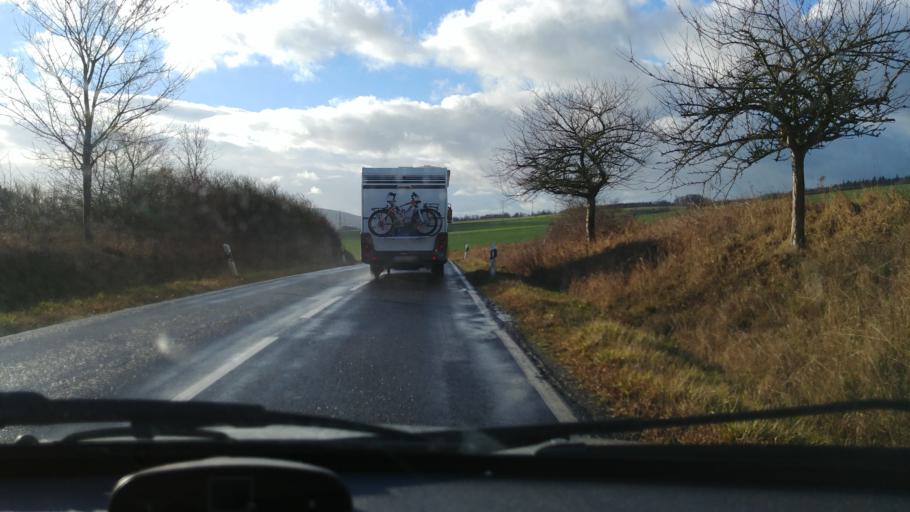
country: DE
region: Hesse
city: Taunusstein
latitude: 50.1655
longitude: 8.1816
